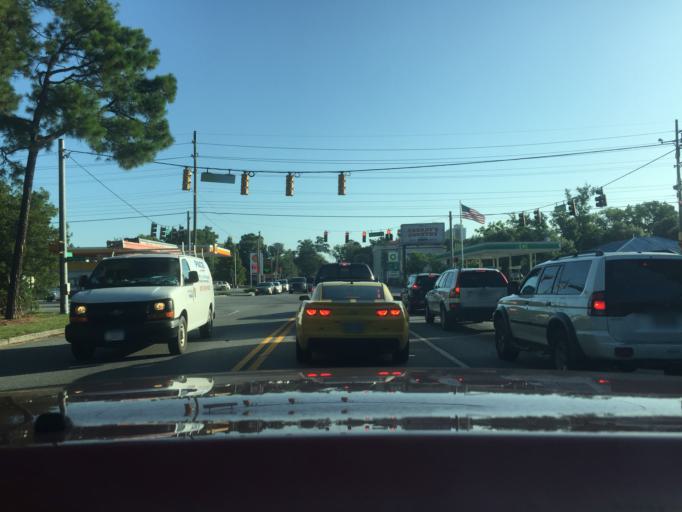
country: US
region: Georgia
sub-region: Chatham County
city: Thunderbolt
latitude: 32.0240
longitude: -81.0948
